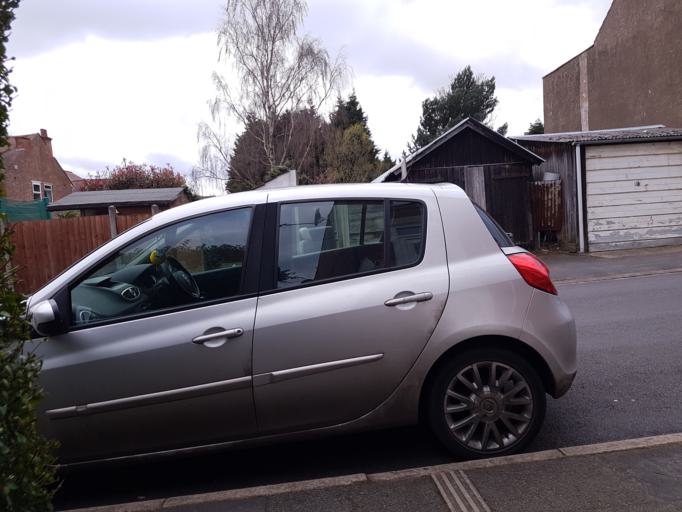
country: GB
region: England
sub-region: Leicestershire
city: Earl Shilton
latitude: 52.5765
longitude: -1.3091
